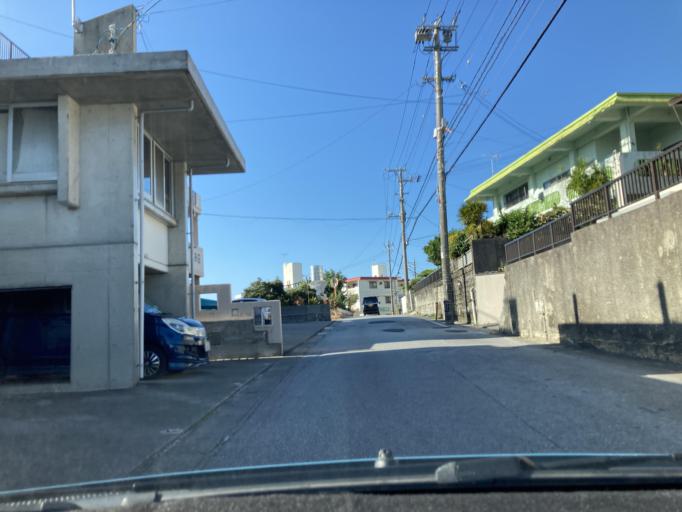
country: JP
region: Okinawa
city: Ginowan
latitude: 26.2505
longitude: 127.7545
